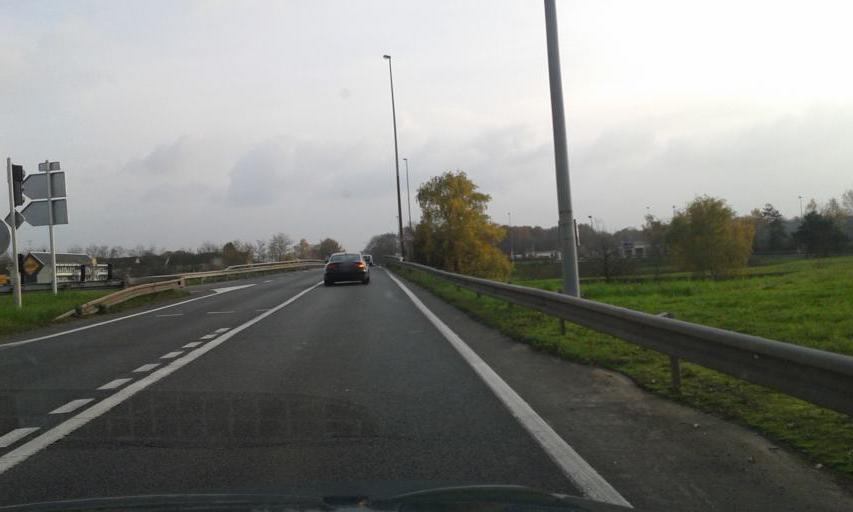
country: FR
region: Centre
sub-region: Departement du Loiret
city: Saran
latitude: 47.9493
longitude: 1.8647
